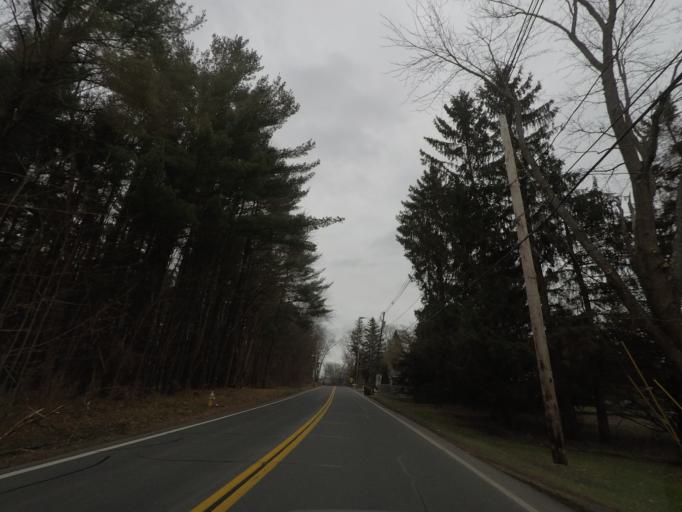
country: US
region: New York
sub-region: Schenectady County
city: Niskayuna
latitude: 42.7769
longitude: -73.8850
